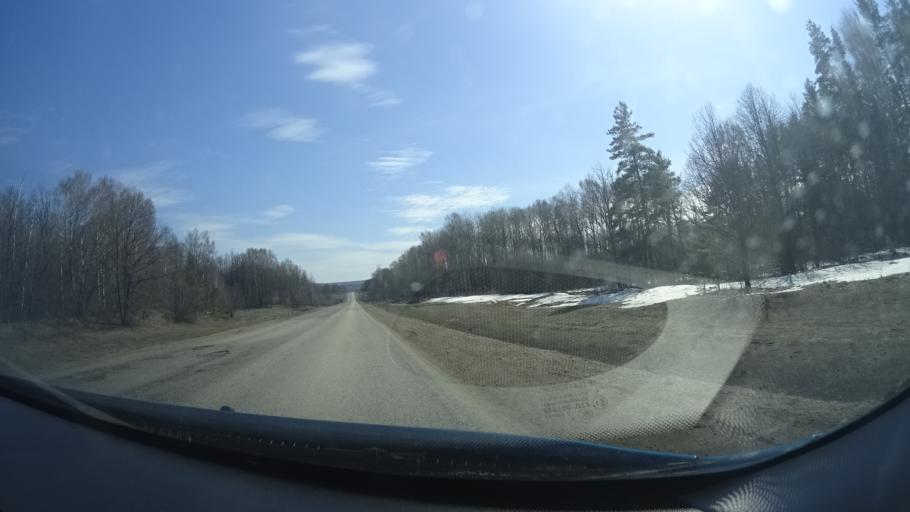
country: RU
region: Bashkortostan
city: Oktyabr'skiy
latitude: 54.4569
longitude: 53.5840
